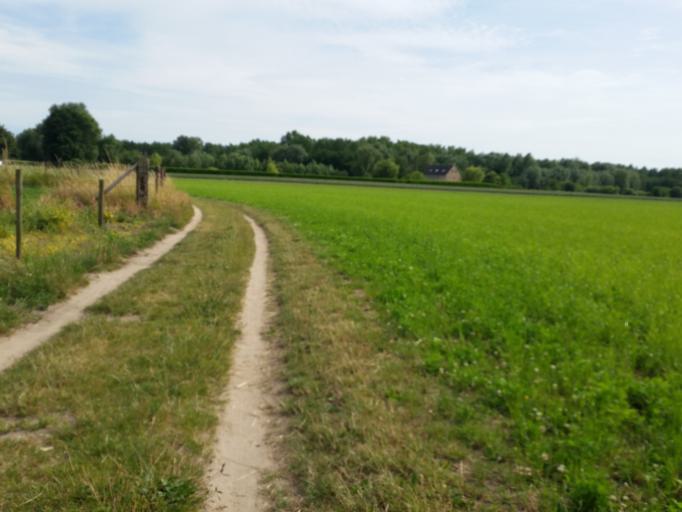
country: BE
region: Flanders
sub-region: Provincie Antwerpen
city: Puurs
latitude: 51.0982
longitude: 4.3029
